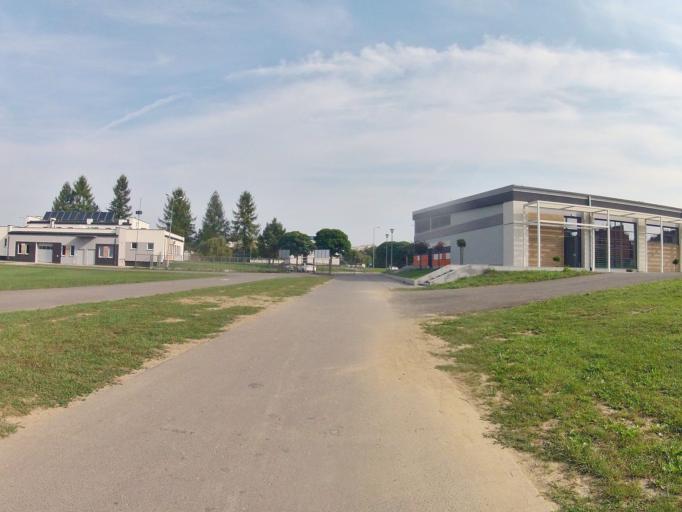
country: PL
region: Subcarpathian Voivodeship
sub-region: Powiat jasielski
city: Jaslo
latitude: 49.7430
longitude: 21.4565
